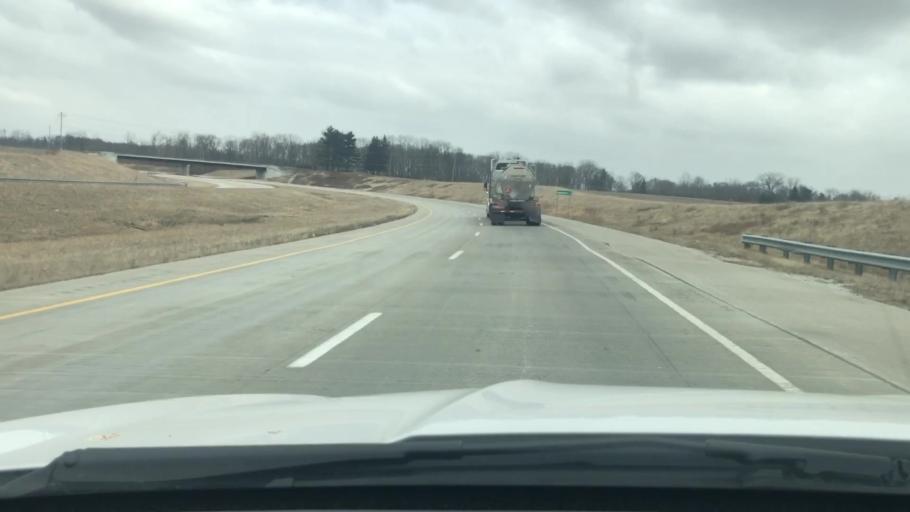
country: US
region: Indiana
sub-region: Carroll County
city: Delphi
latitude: 40.5729
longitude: -86.6482
